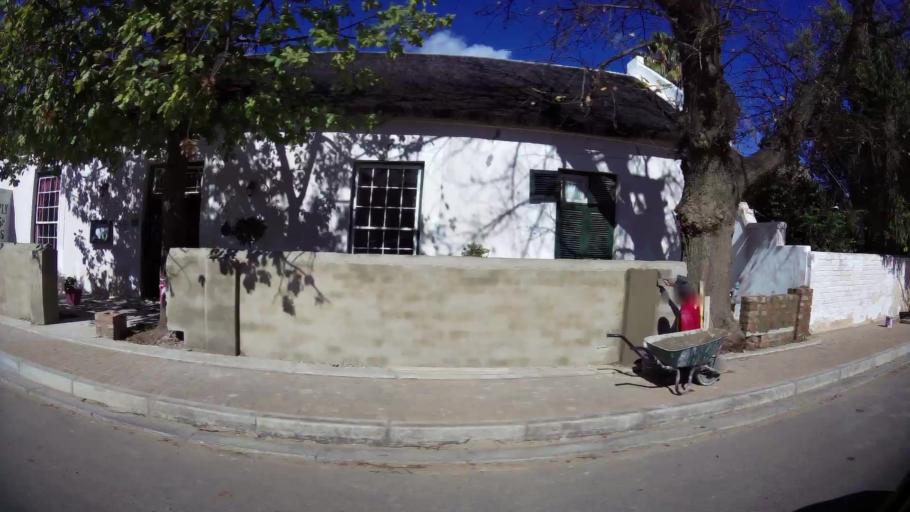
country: ZA
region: Western Cape
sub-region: Cape Winelands District Municipality
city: Ashton
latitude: -33.7891
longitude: 20.1216
